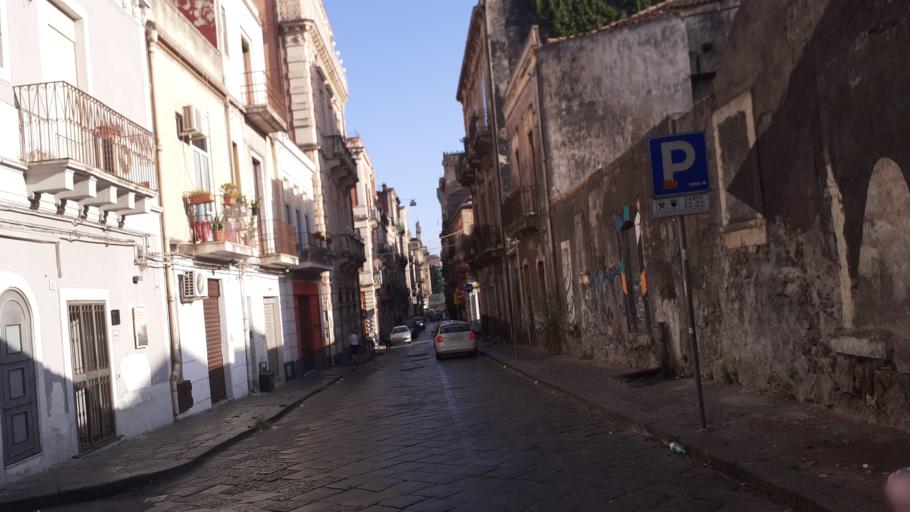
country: IT
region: Sicily
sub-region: Catania
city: Catania
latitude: 37.5126
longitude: 15.0880
